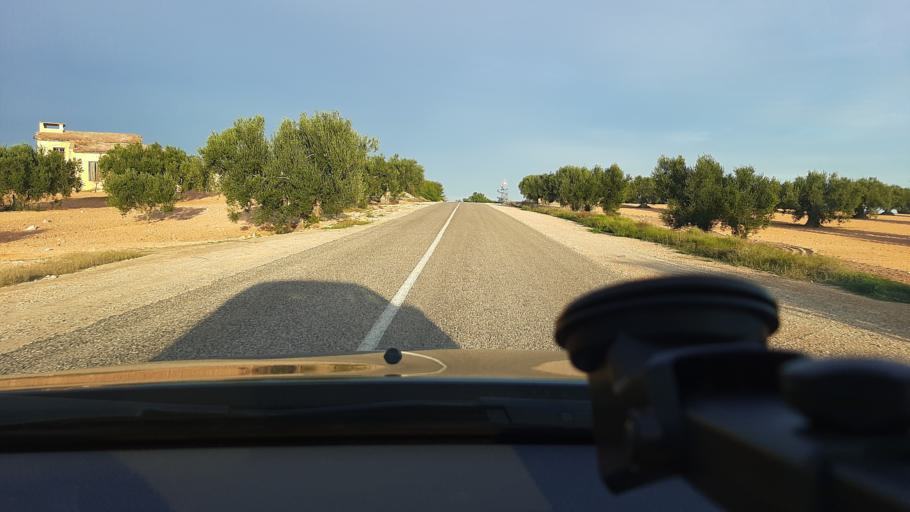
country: TN
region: Safaqis
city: Sfax
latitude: 34.9570
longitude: 10.5397
